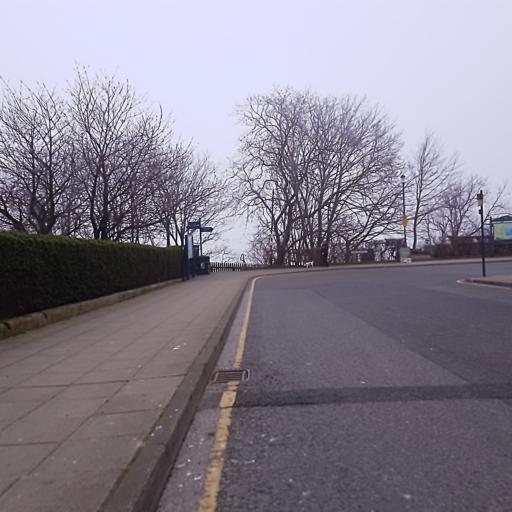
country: GB
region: England
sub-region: North Yorkshire
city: Filey
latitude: 54.2083
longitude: -0.2867
